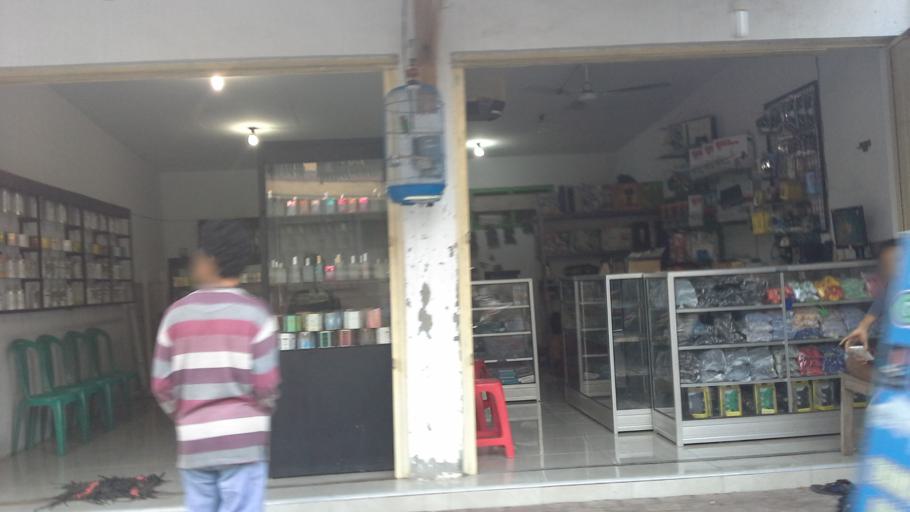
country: ID
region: East Java
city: Bondowoso
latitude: -7.9242
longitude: 113.8267
